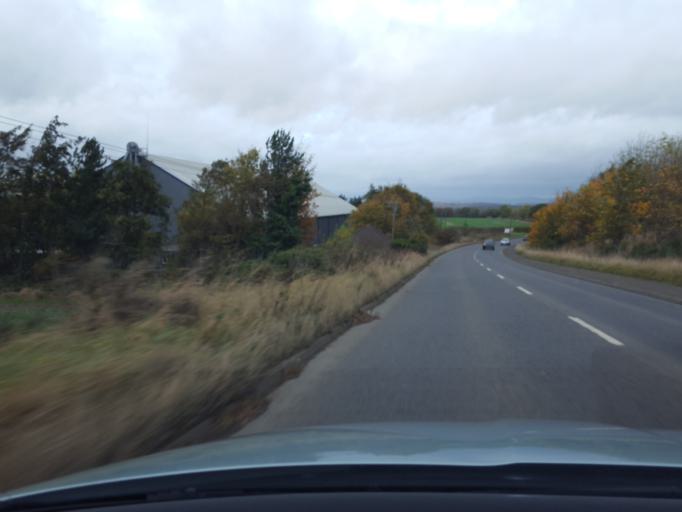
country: GB
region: Scotland
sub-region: Edinburgh
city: Newbridge
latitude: 55.9141
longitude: -3.4078
